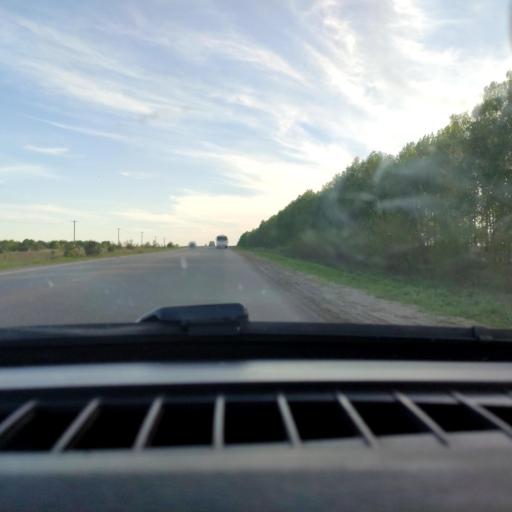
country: RU
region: Kursk
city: Gorshechnoye
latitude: 51.4601
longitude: 37.9234
